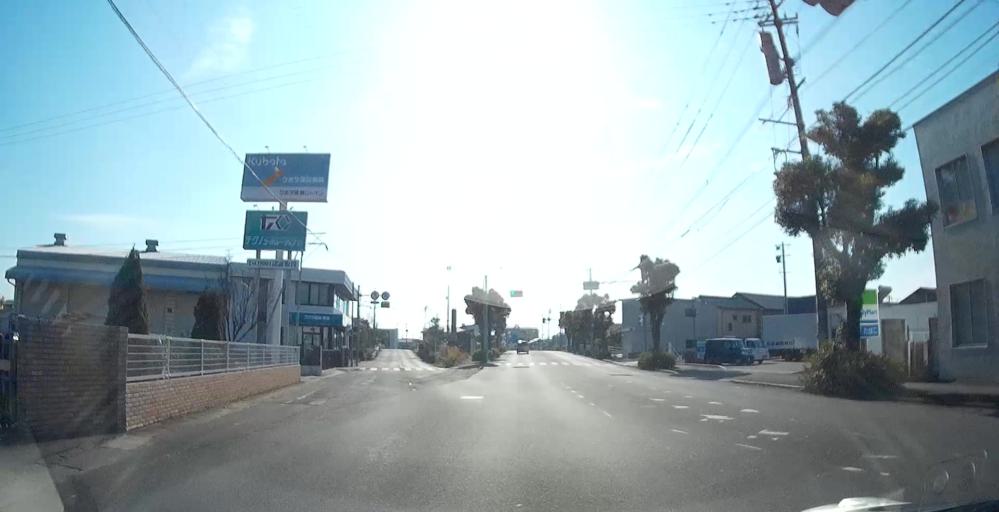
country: JP
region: Kumamoto
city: Kumamoto
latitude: 32.7466
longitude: 130.6831
